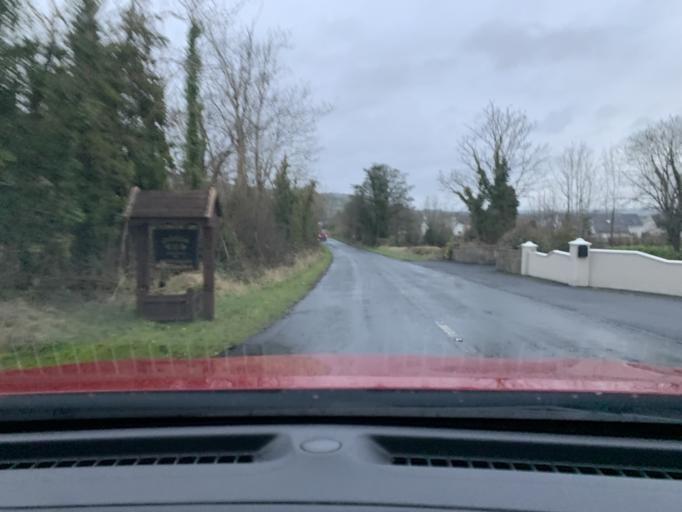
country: IE
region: Connaught
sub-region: Roscommon
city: Boyle
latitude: 54.0246
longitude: -8.3295
